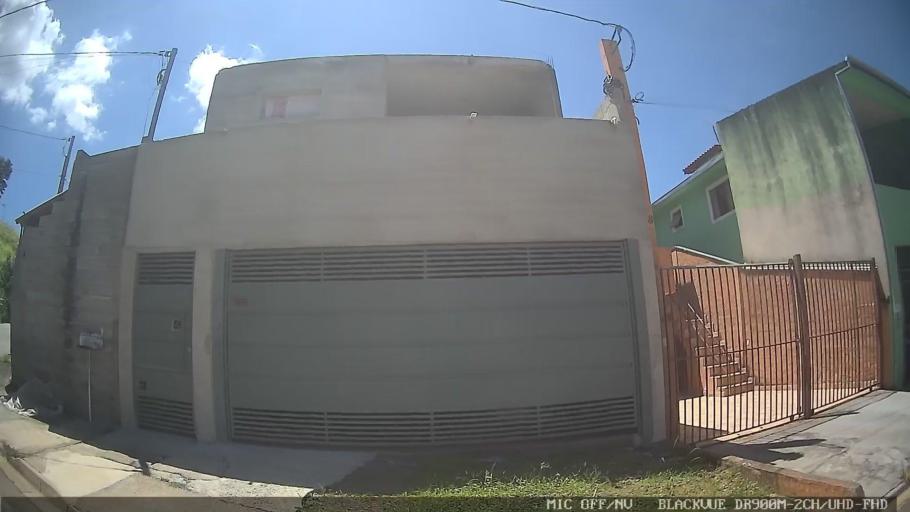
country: BR
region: Sao Paulo
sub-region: Atibaia
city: Atibaia
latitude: -23.1006
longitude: -46.5655
